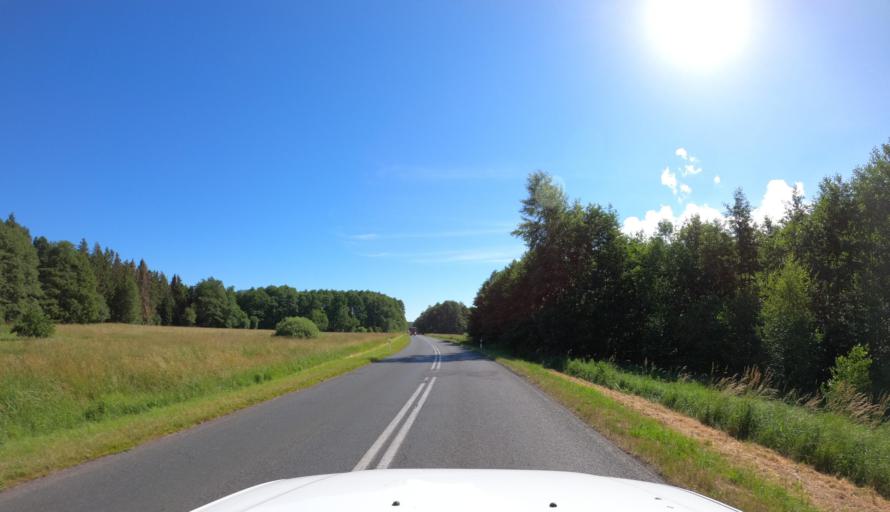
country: PL
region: West Pomeranian Voivodeship
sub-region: Powiat gryficki
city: Pobierowo
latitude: 54.0383
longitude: 14.8576
